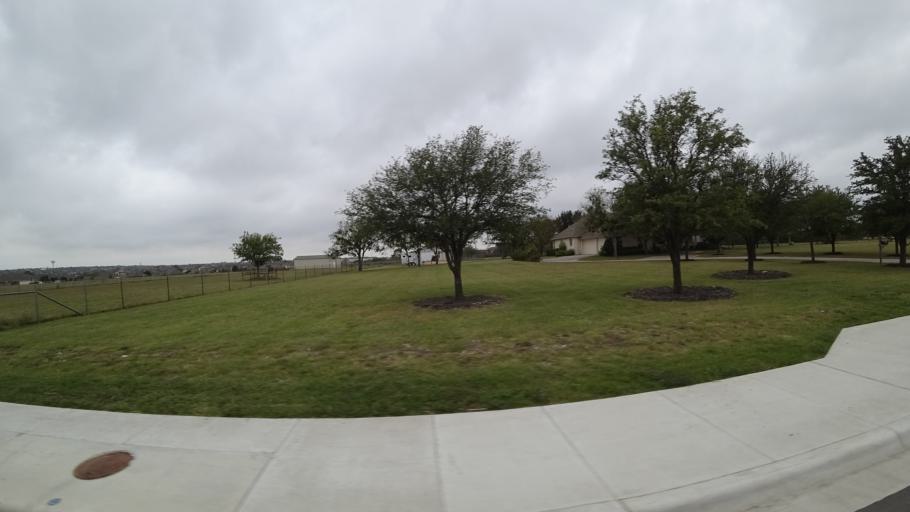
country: US
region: Texas
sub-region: Travis County
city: Windemere
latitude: 30.4791
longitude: -97.6166
